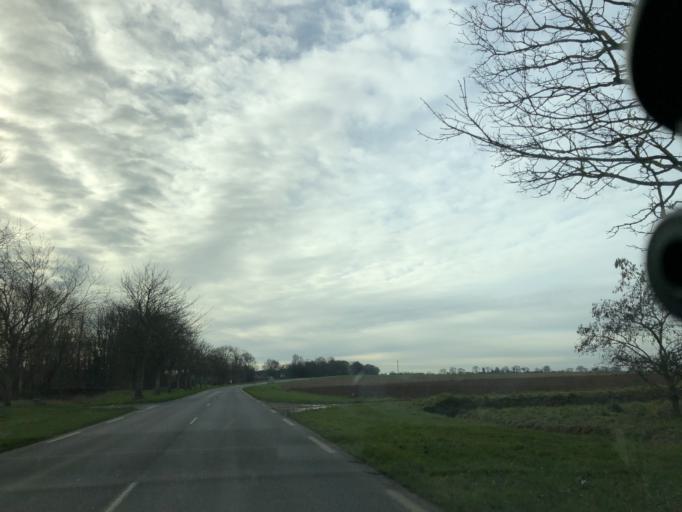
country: FR
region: Lower Normandy
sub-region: Departement du Calvados
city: Hermanville-sur-Mer
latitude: 49.2908
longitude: -0.3164
